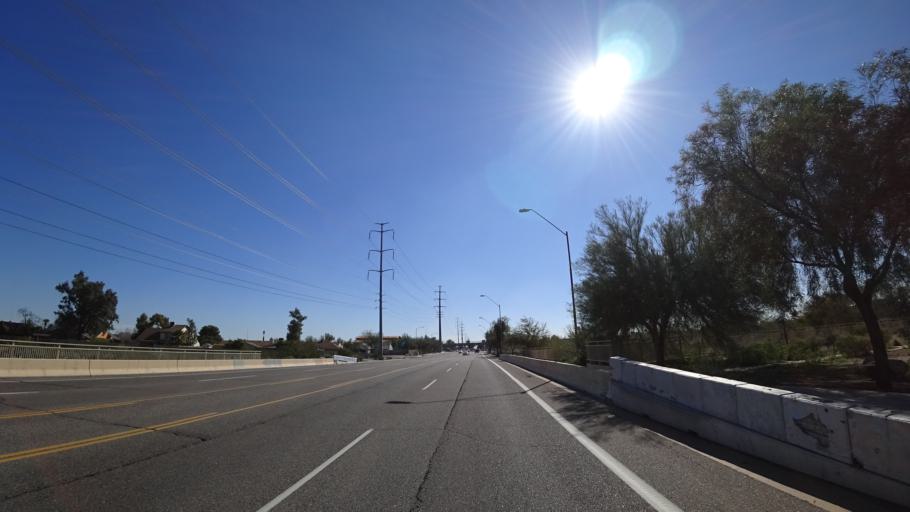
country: US
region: Arizona
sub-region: Maricopa County
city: Peoria
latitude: 33.6727
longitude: -112.1348
